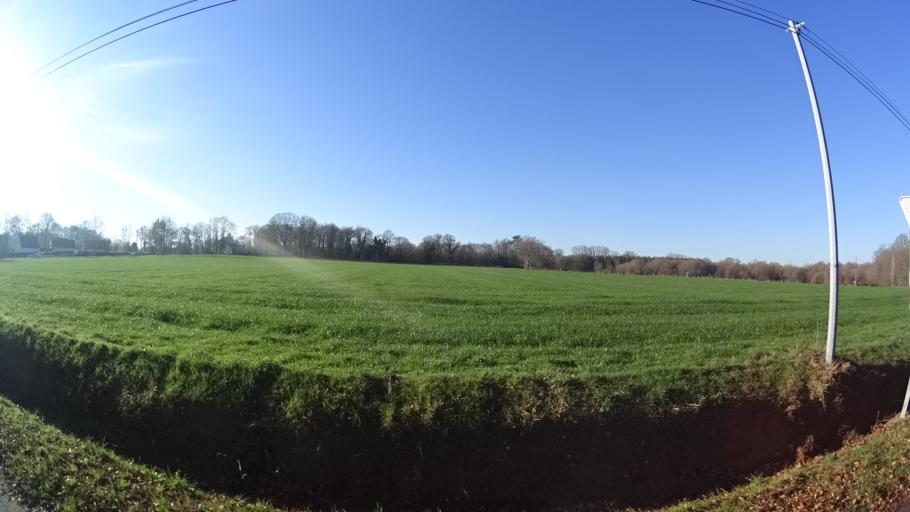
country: FR
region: Brittany
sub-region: Departement du Morbihan
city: Allaire
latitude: 47.6355
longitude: -2.1465
